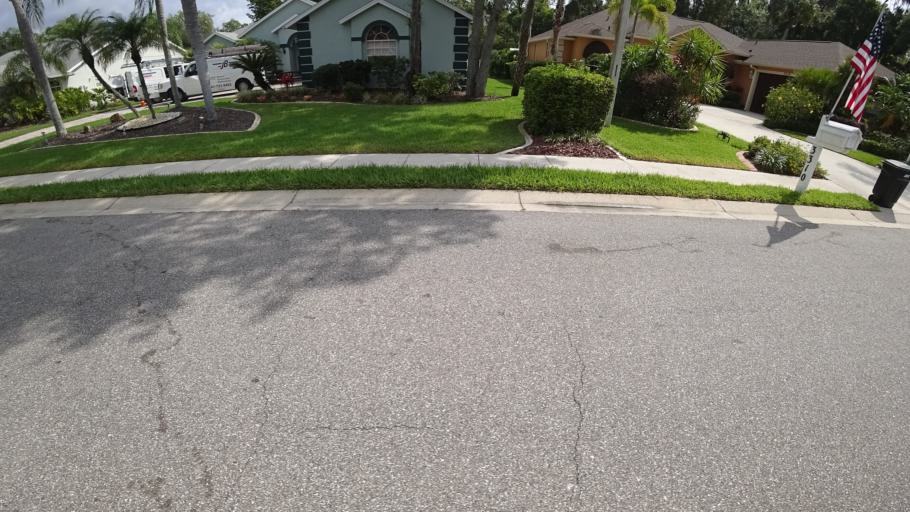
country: US
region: Florida
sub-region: Manatee County
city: Ellenton
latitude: 27.5437
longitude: -82.4509
